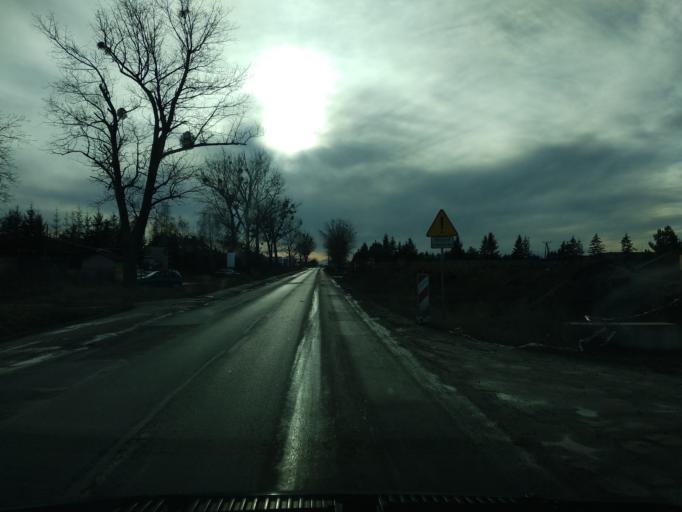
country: PL
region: Lower Silesian Voivodeship
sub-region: Powiat wroclawski
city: Zerniki Wroclawskie
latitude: 51.0472
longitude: 17.0603
